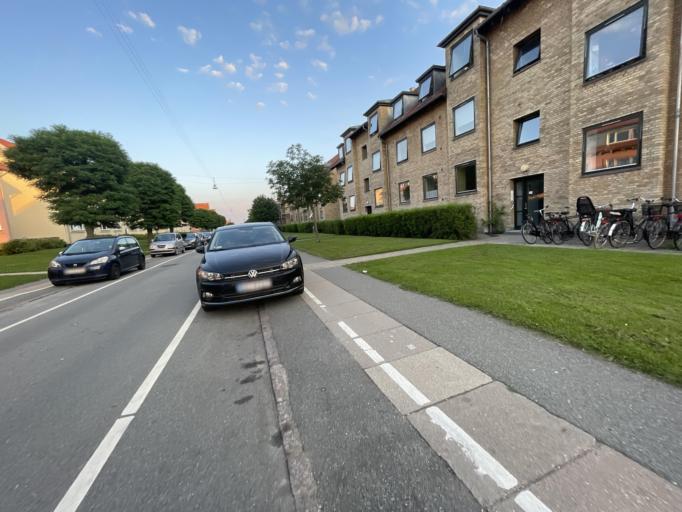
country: DK
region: Capital Region
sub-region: Kobenhavn
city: Vanlose
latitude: 55.6949
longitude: 12.4996
